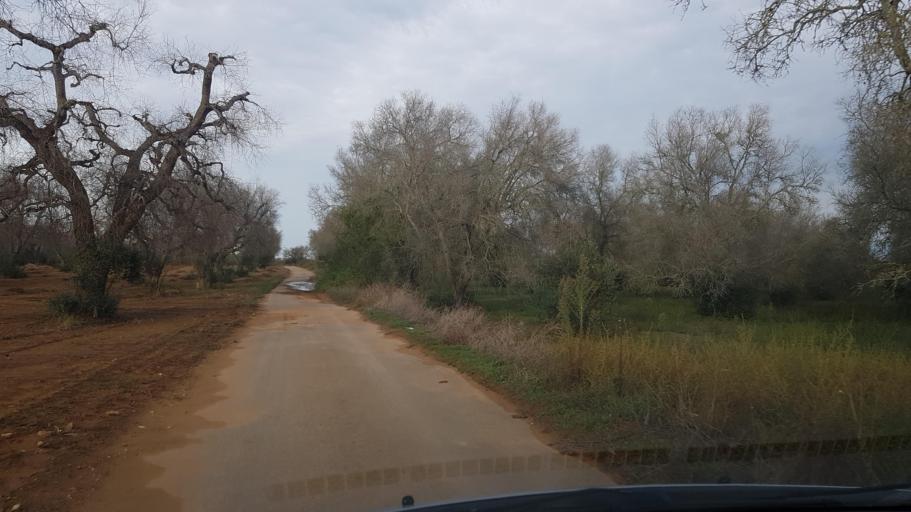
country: IT
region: Apulia
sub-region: Provincia di Brindisi
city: Torchiarolo
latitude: 40.4994
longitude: 18.0827
